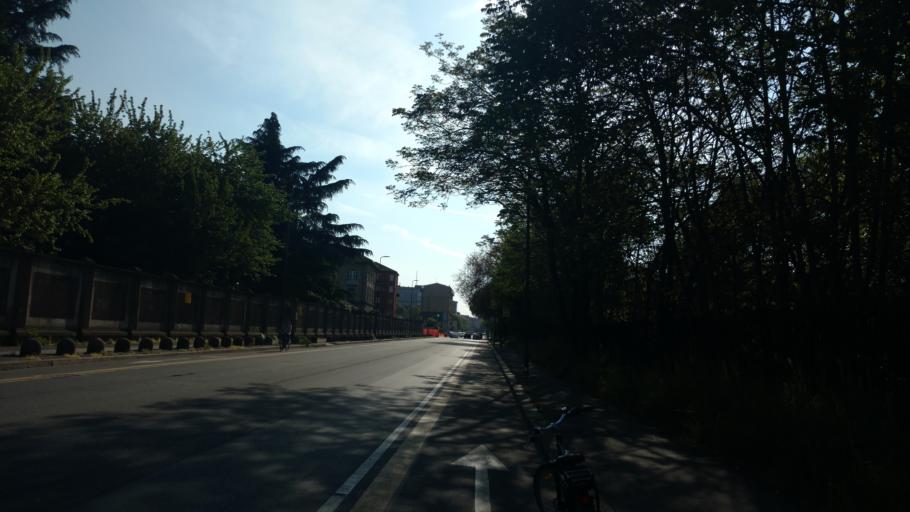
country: IT
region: Lombardy
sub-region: Citta metropolitana di Milano
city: Romano Banco
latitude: 45.4620
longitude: 9.1225
